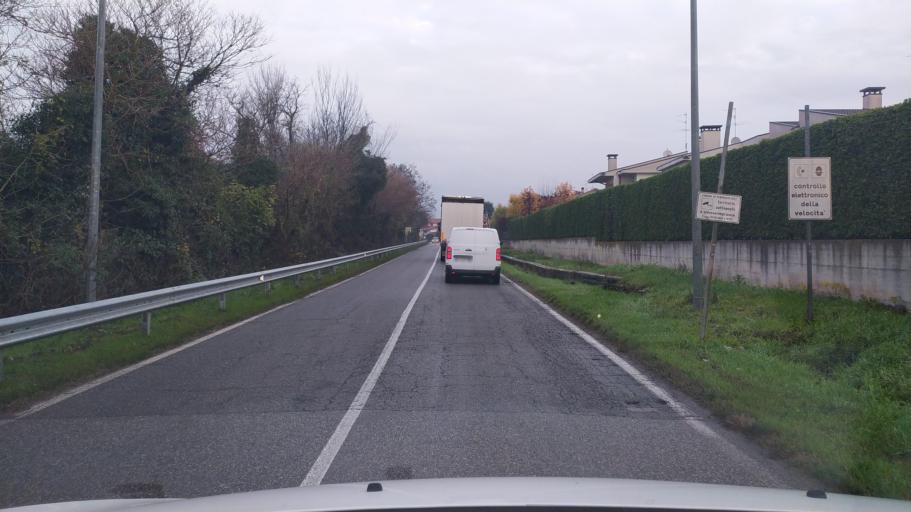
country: IT
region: Lombardy
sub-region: Provincia di Brescia
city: Pontoglio
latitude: 45.5632
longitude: 9.8600
